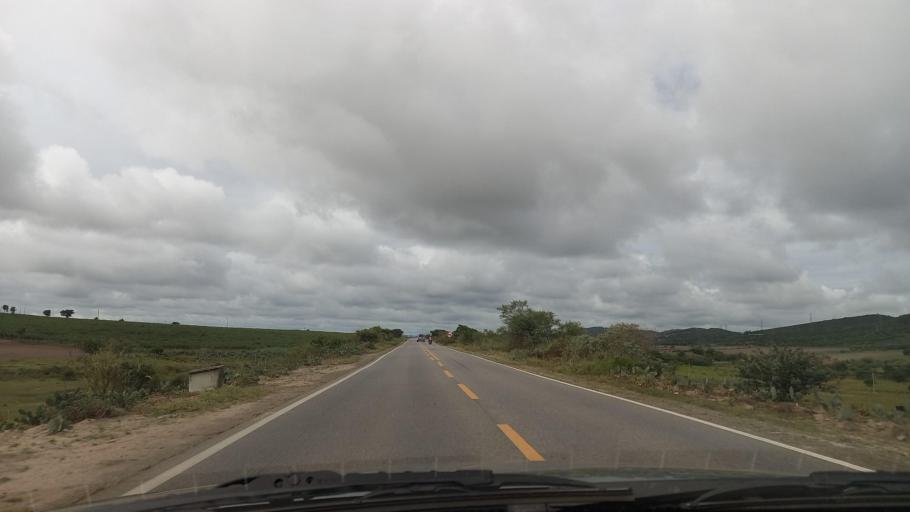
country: BR
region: Pernambuco
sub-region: Sao Joao
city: Sao Joao
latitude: -8.8784
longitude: -36.3971
